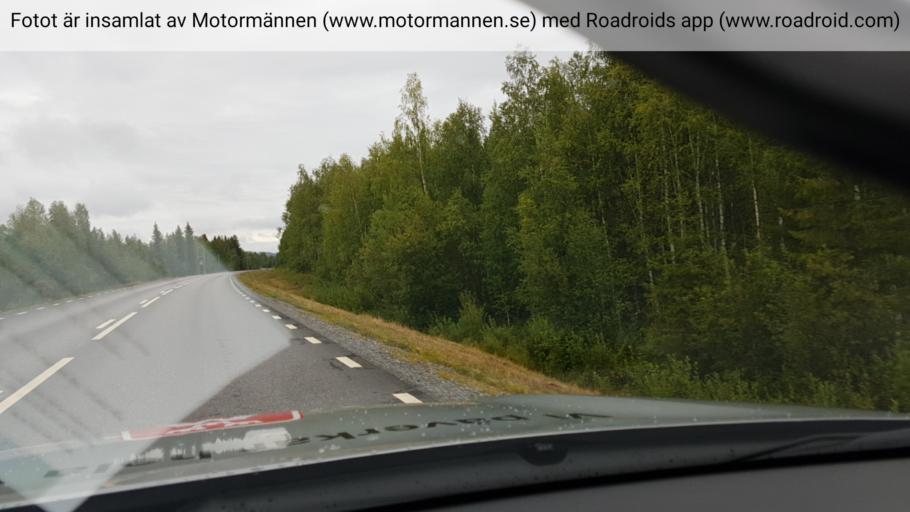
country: SE
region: Norrbotten
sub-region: Alvsbyns Kommun
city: AElvsbyn
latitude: 66.2761
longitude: 20.8220
